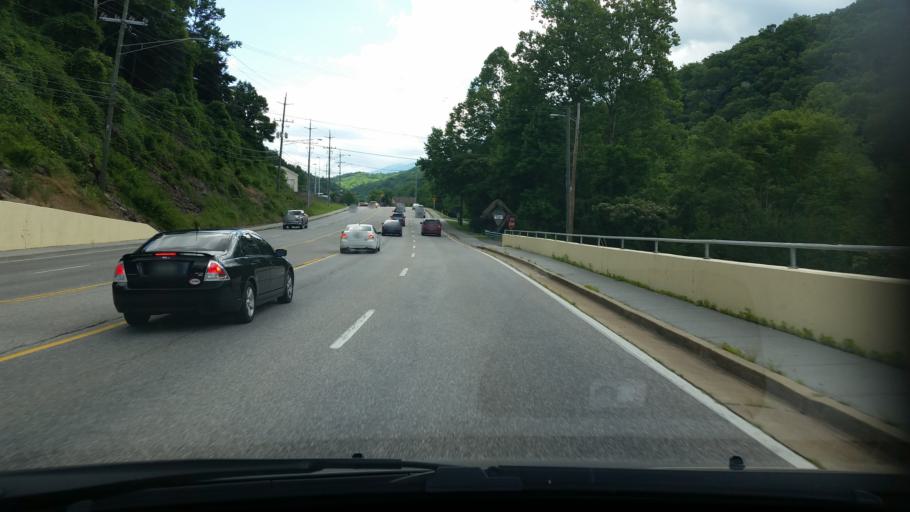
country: US
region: Tennessee
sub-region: Sevier County
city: Gatlinburg
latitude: 35.7261
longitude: -83.4834
